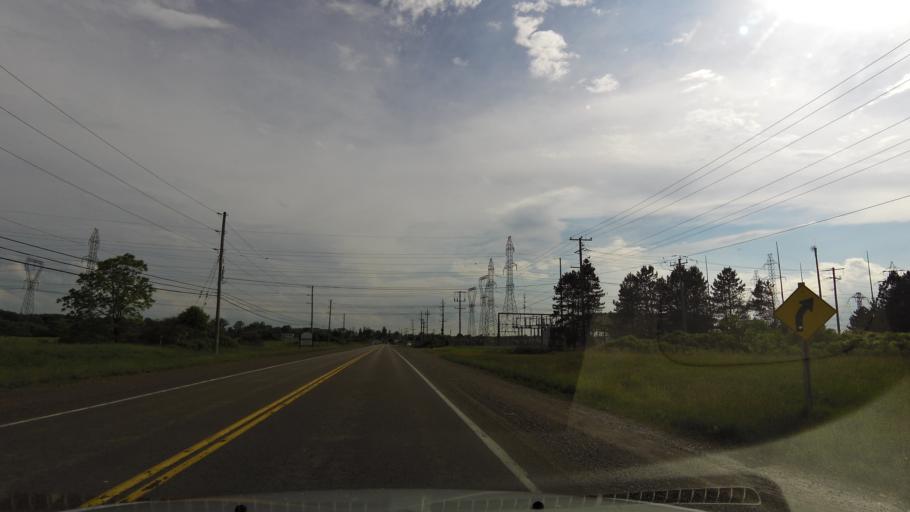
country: CA
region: Ontario
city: Ancaster
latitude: 43.0519
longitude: -79.9707
